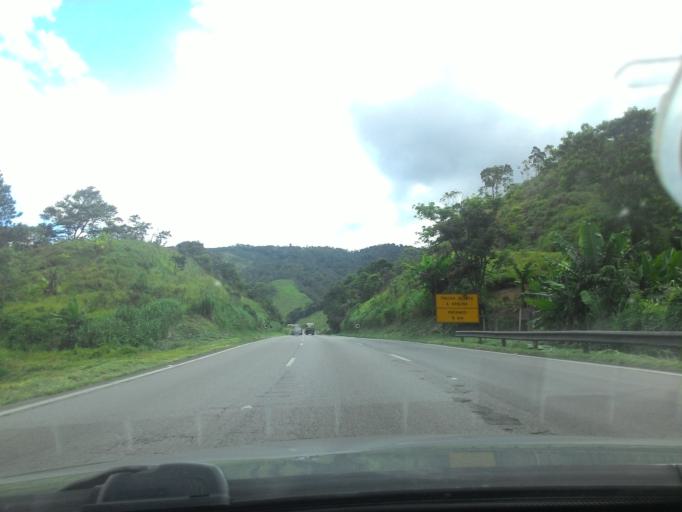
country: BR
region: Sao Paulo
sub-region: Cajati
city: Cajati
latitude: -24.8748
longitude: -48.2253
